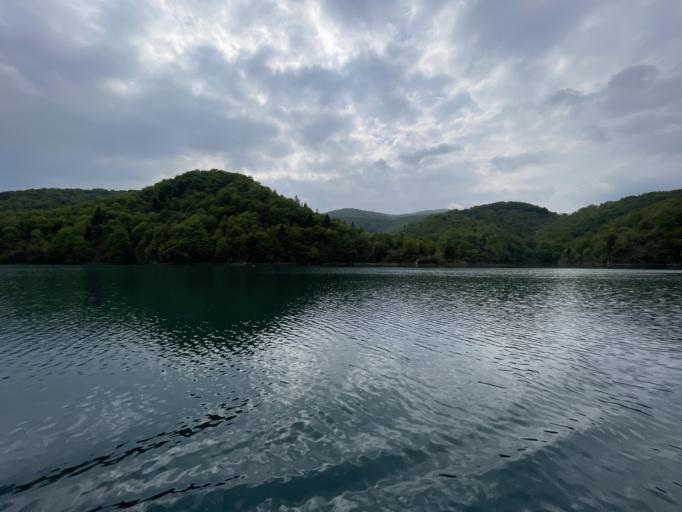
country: HR
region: Licko-Senjska
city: Jezerce
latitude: 44.8913
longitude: 15.6048
